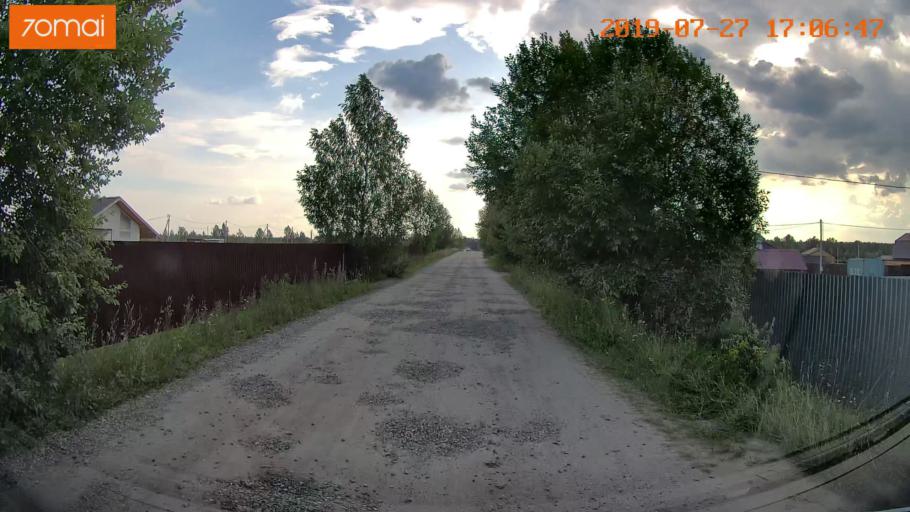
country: RU
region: Ivanovo
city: Novo-Talitsy
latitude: 57.0860
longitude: 40.8397
